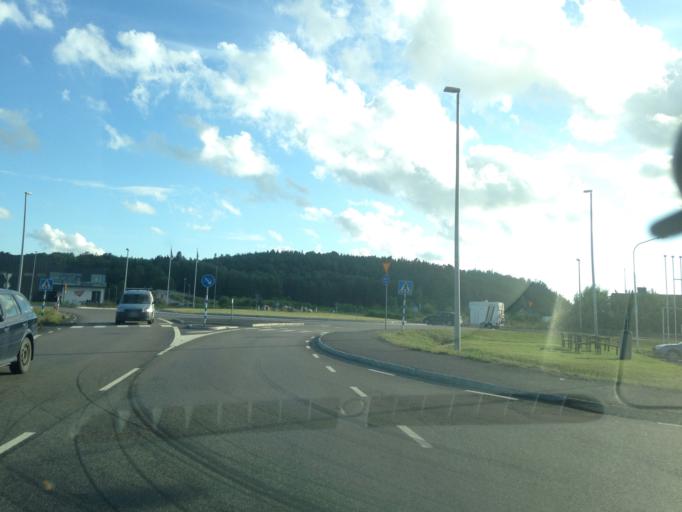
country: SE
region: Halland
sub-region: Kungsbacka Kommun
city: Fjaeras kyrkby
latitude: 57.4354
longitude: 12.1550
